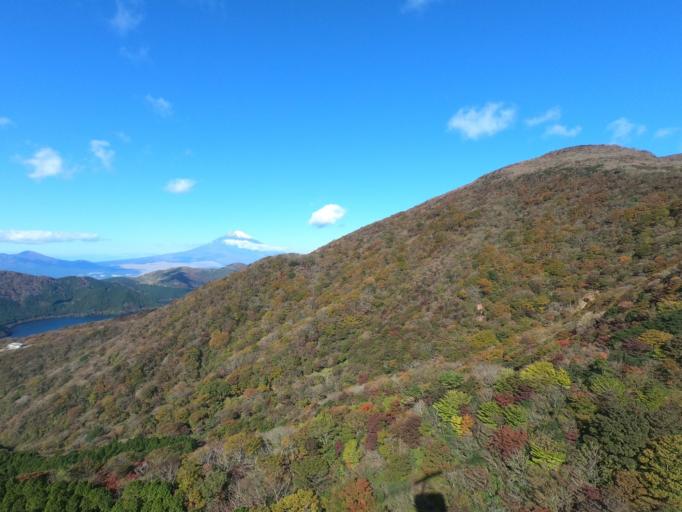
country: JP
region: Kanagawa
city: Hakone
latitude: 35.2201
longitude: 139.0191
